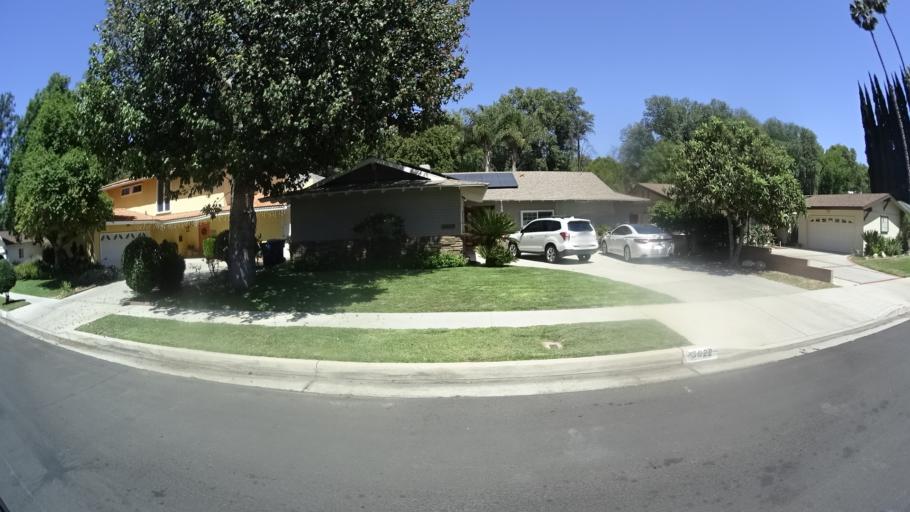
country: US
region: California
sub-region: Los Angeles County
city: Van Nuys
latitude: 34.1911
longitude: -118.4968
